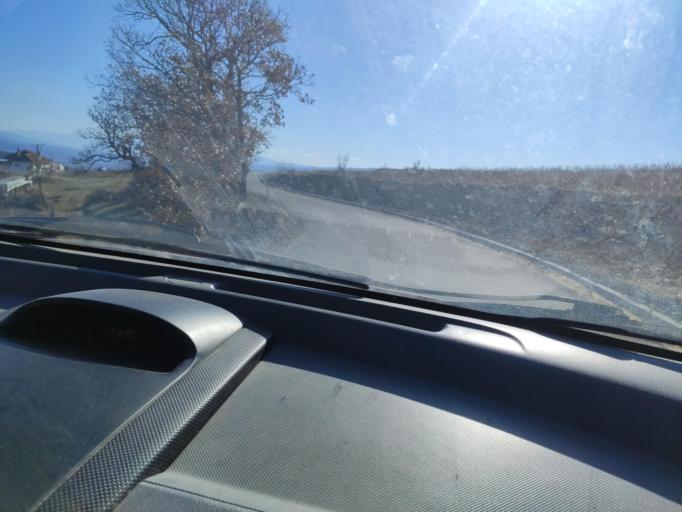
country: MK
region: Radovis
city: Radovish
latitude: 41.6618
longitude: 22.4098
